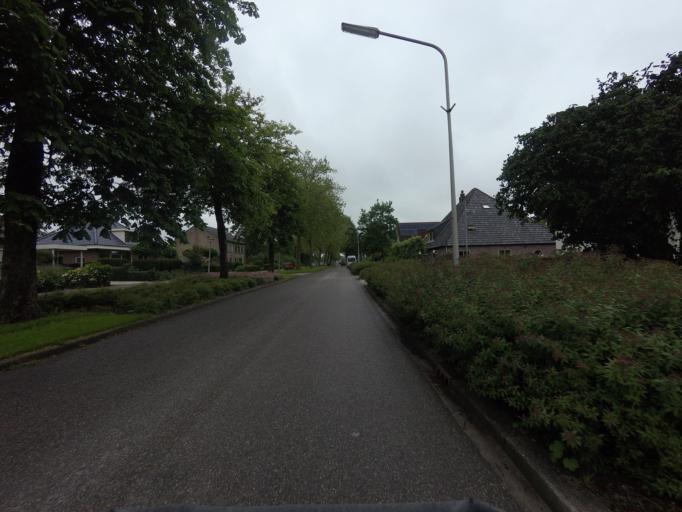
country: NL
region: North Holland
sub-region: Gemeente Opmeer
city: Opmeer
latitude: 52.7578
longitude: 4.8987
